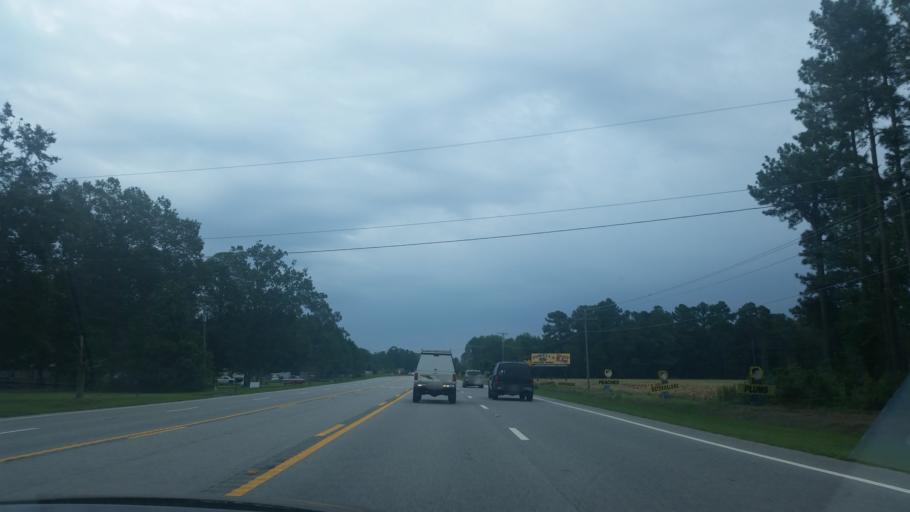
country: US
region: North Carolina
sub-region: Currituck County
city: Currituck
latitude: 36.4563
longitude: -76.0888
